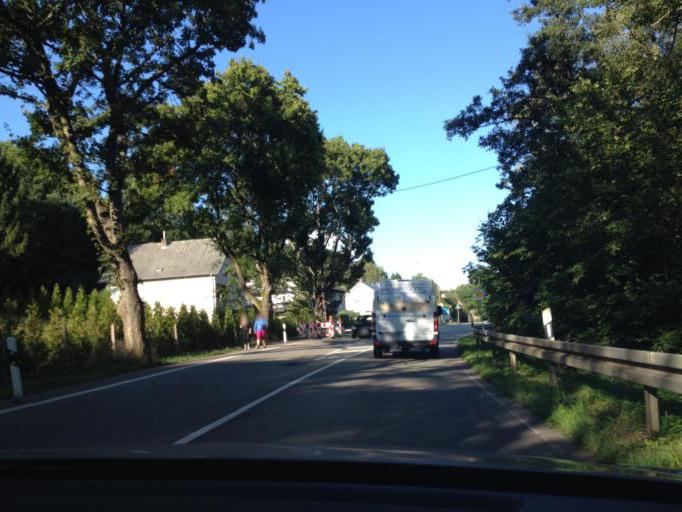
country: DE
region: Saarland
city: Wadern
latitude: 49.4825
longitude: 6.9125
